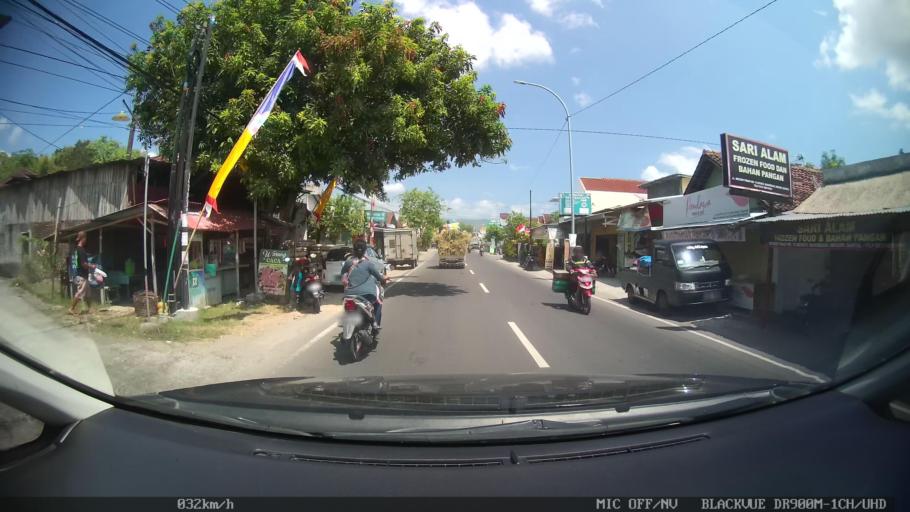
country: ID
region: Daerah Istimewa Yogyakarta
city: Sewon
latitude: -7.9137
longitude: 110.3824
